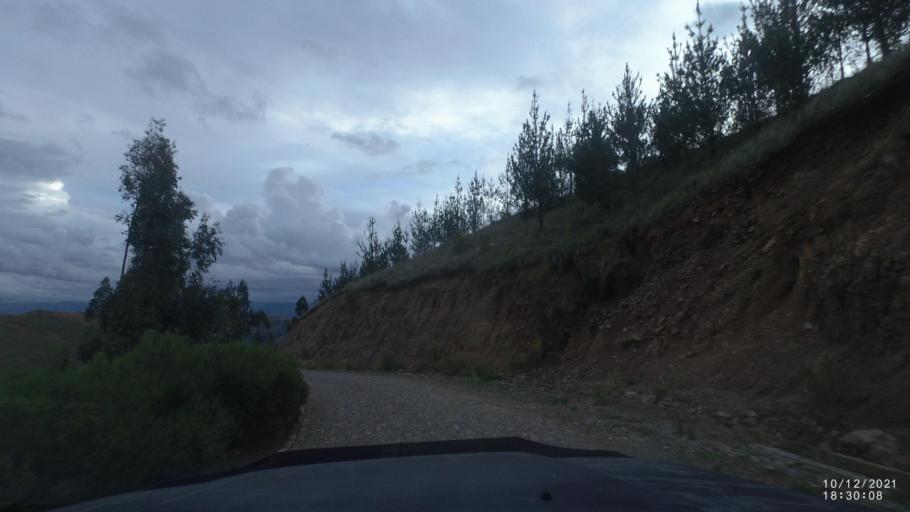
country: BO
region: Cochabamba
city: Tarata
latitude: -17.8136
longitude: -65.9803
